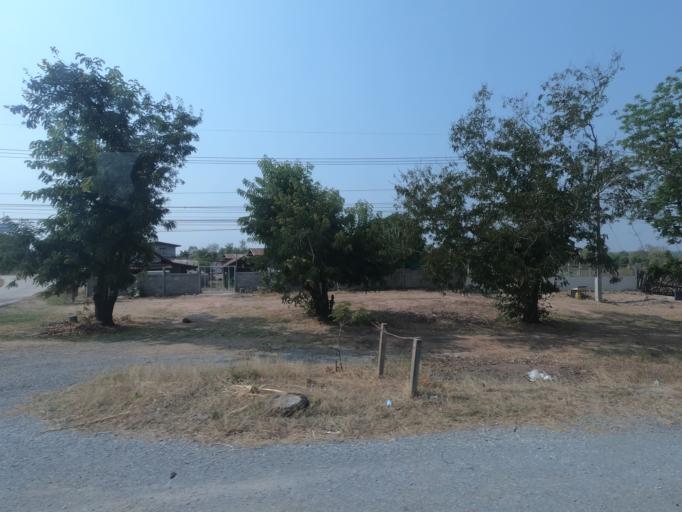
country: TH
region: Nakhon Ratchasima
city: Non Daeng
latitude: 15.4016
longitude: 102.4733
